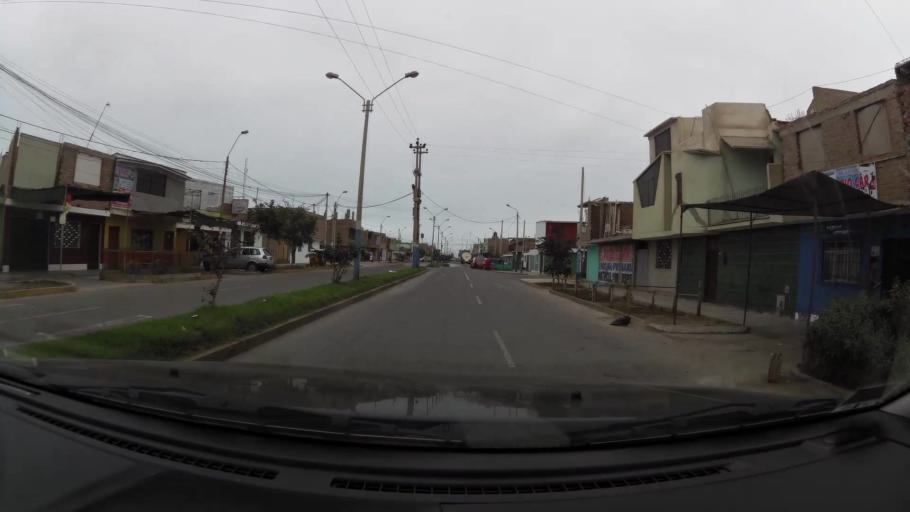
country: PE
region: Ica
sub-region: Provincia de Pisco
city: Pisco
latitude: -13.7153
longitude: -76.2087
